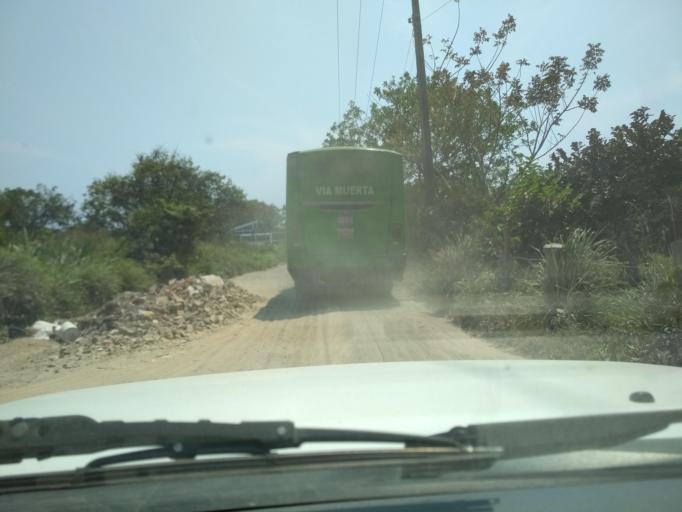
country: MX
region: Veracruz
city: Boca del Rio
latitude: 19.0973
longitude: -96.1244
